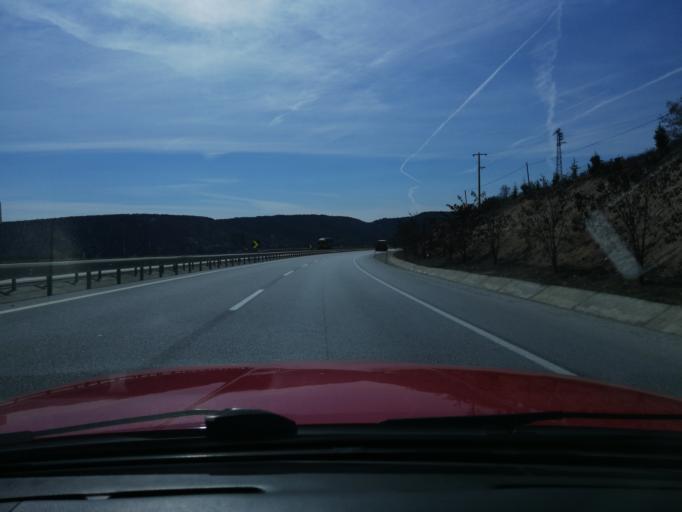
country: TR
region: Kuetahya
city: Sabuncu
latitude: 39.6185
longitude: 30.1568
